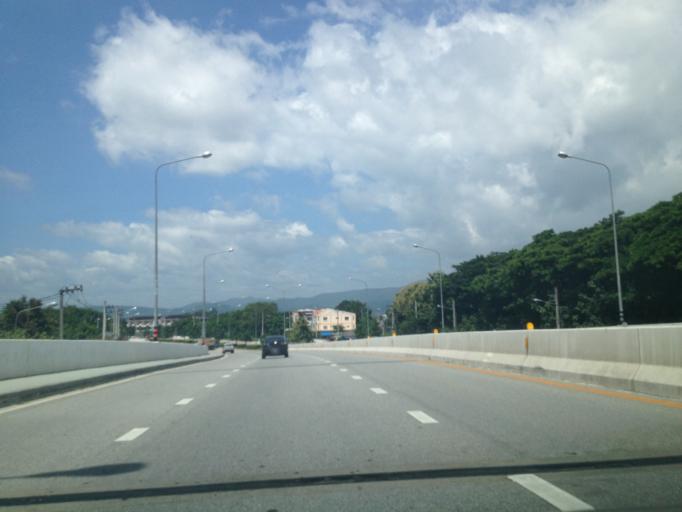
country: TH
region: Chiang Mai
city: Chiang Mai
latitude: 18.7459
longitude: 98.9843
